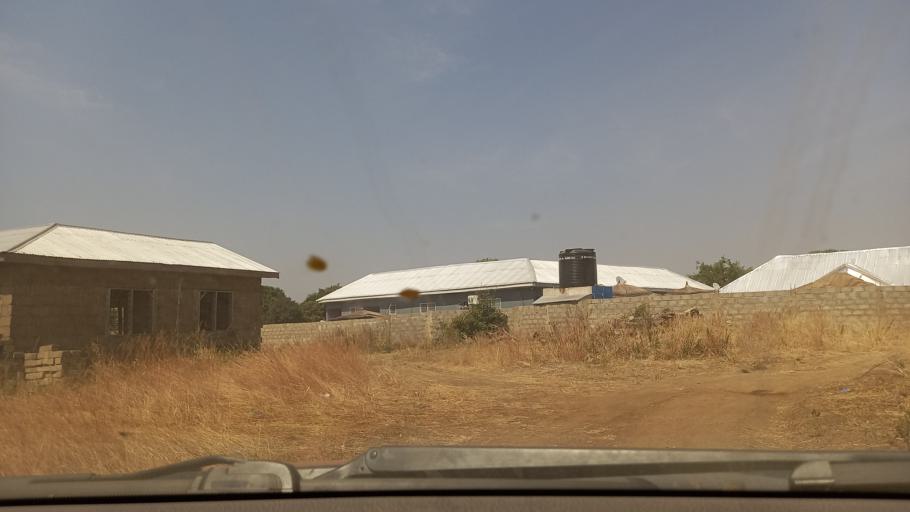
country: GH
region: Upper East
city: Navrongo
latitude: 10.8606
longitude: -1.0866
